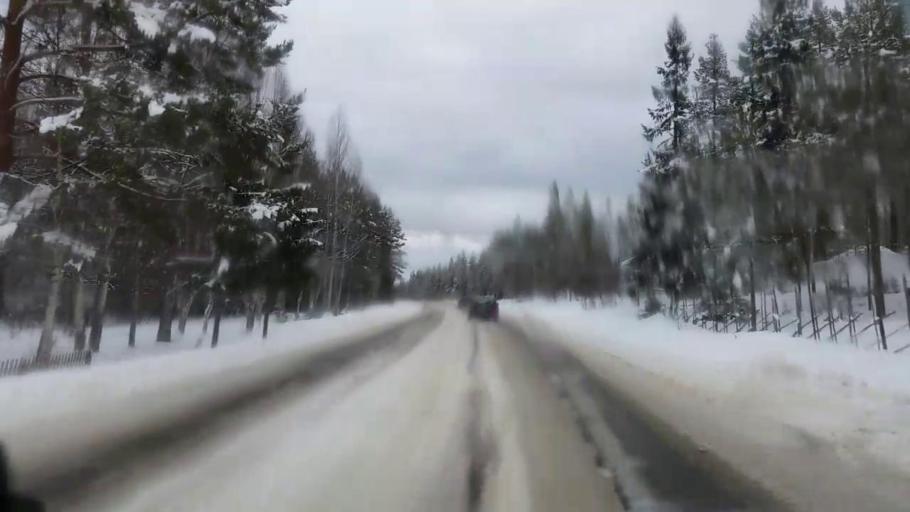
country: SE
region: Vaesternorrland
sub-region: Ange Kommun
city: Ange
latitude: 62.0511
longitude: 15.1457
